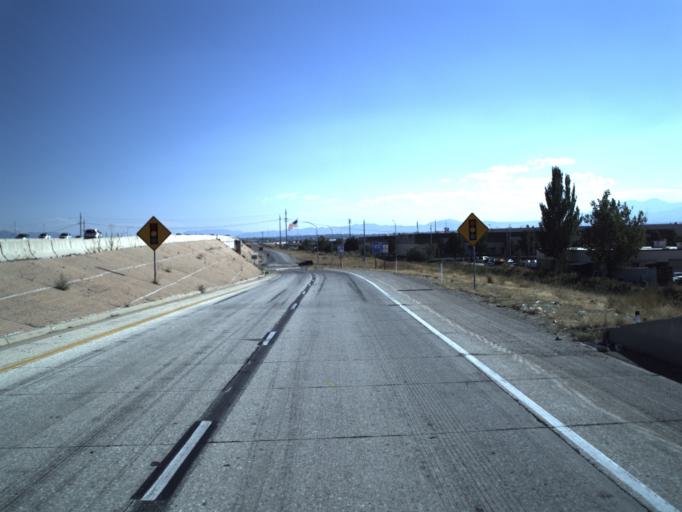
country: US
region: Utah
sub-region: Salt Lake County
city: Salt Lake City
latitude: 40.7430
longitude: -111.9495
